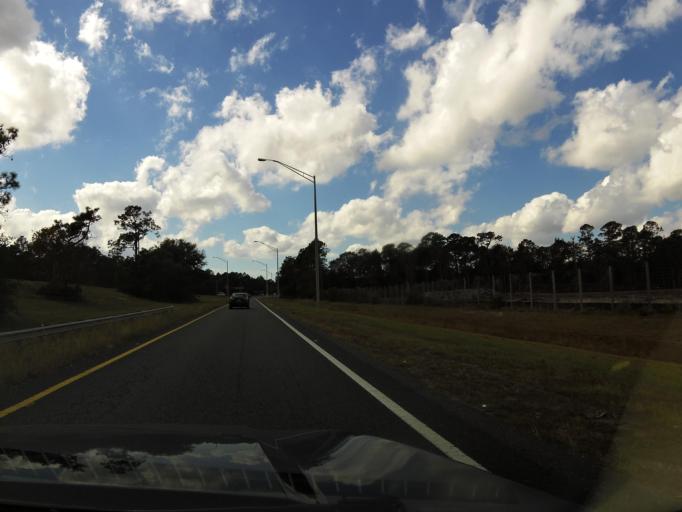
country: US
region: Florida
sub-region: Saint Johns County
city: Ponte Vedra Beach
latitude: 30.2521
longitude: -81.4681
